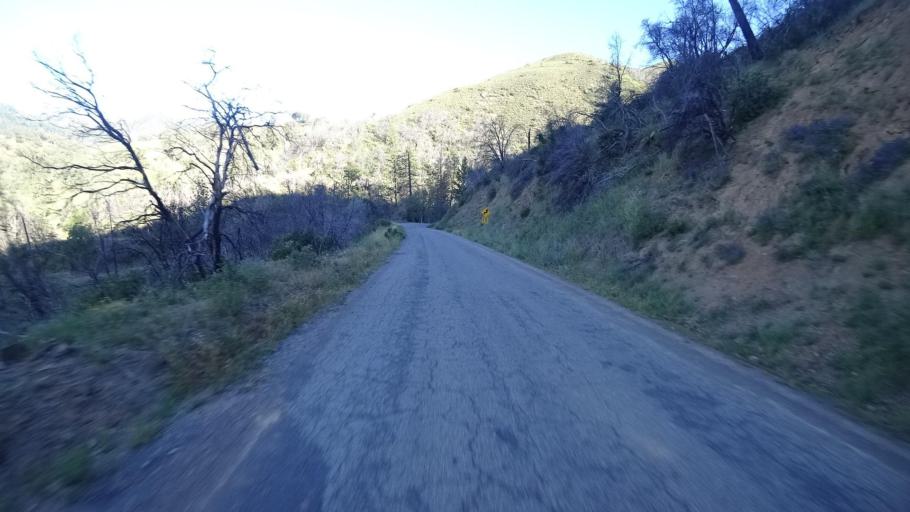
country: US
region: California
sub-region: Lake County
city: Upper Lake
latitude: 39.2592
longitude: -122.9459
